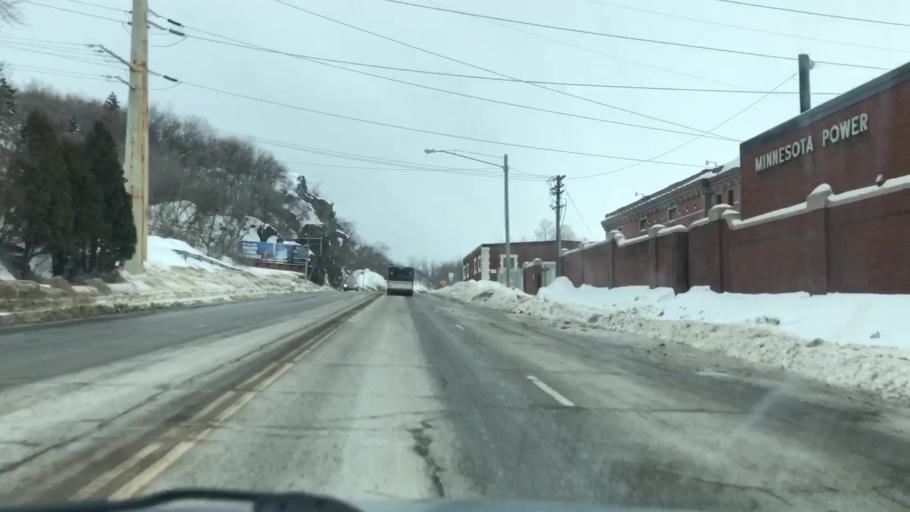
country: US
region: Minnesota
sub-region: Saint Louis County
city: Duluth
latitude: 46.7724
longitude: -92.1173
